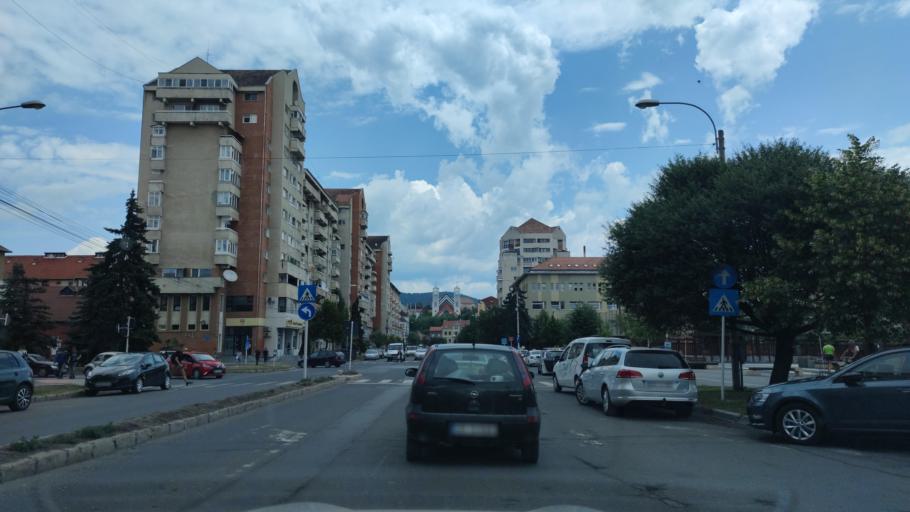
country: RO
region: Harghita
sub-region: Municipiul Miercurea Ciuc
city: Miercurea-Ciuc
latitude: 46.3620
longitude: 25.8014
